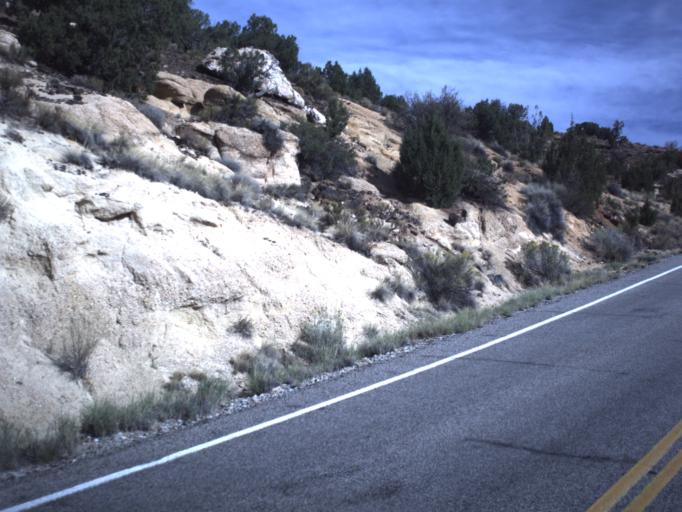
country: US
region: Utah
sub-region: San Juan County
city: Blanding
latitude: 37.4352
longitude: -109.3929
